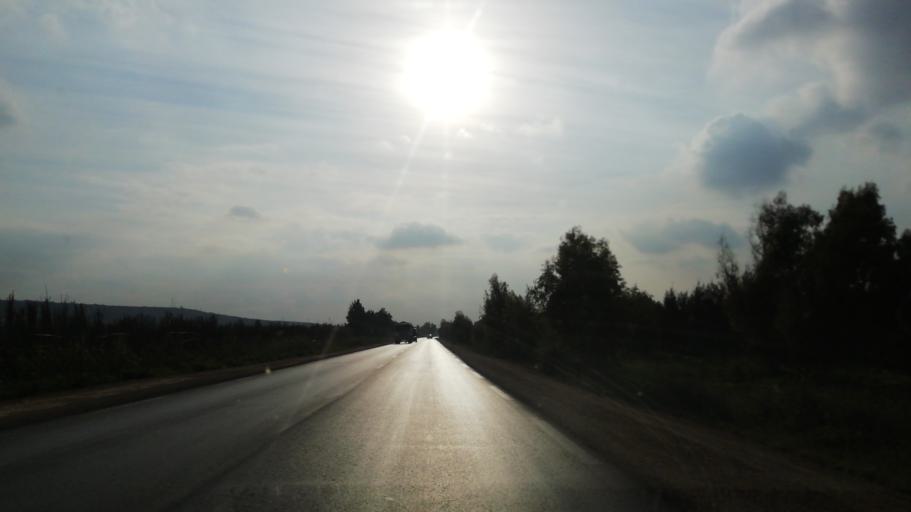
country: DZ
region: Mostaganem
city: Mostaganem
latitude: 35.8433
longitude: 0.0668
